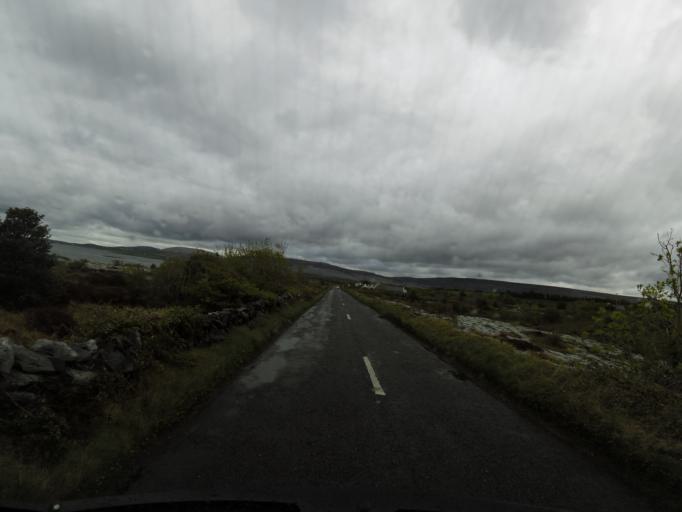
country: IE
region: Connaught
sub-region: County Galway
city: Bearna
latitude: 53.1239
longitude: -9.1717
